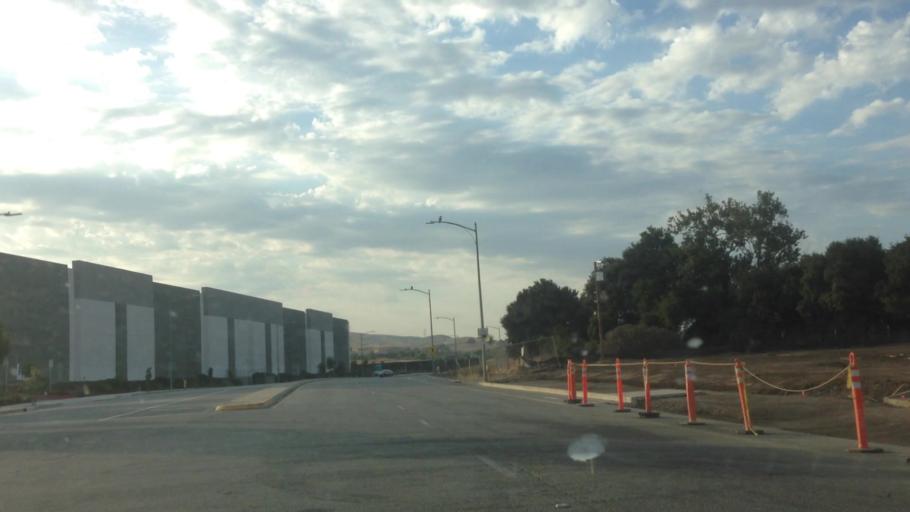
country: US
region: California
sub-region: Santa Clara County
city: Seven Trees
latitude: 37.2564
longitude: -121.7794
